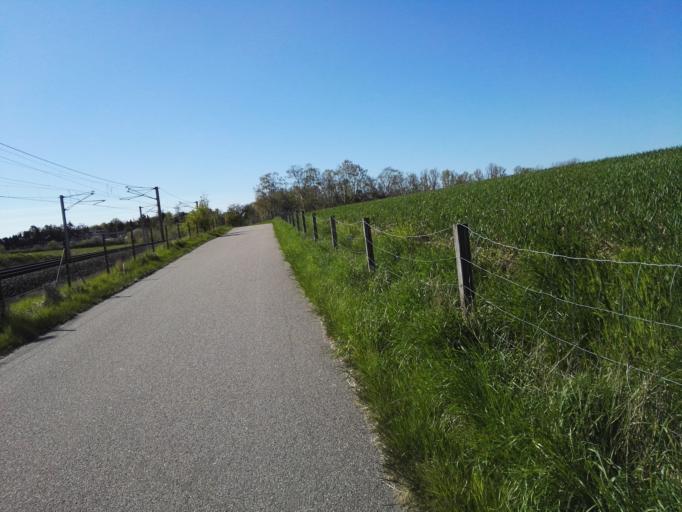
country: DK
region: Capital Region
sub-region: Egedal Kommune
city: Stenlose
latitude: 55.7560
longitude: 12.2058
